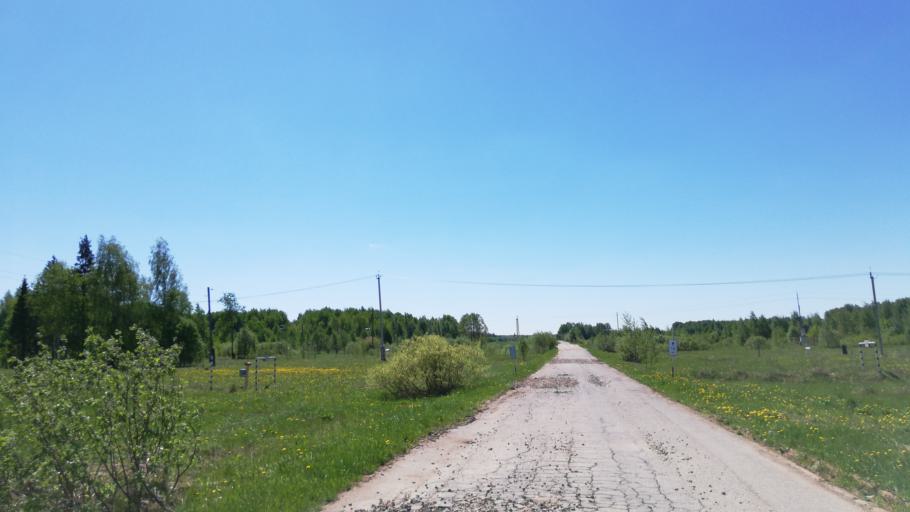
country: RU
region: Ivanovo
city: Pistsovo
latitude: 57.1266
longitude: 40.6017
